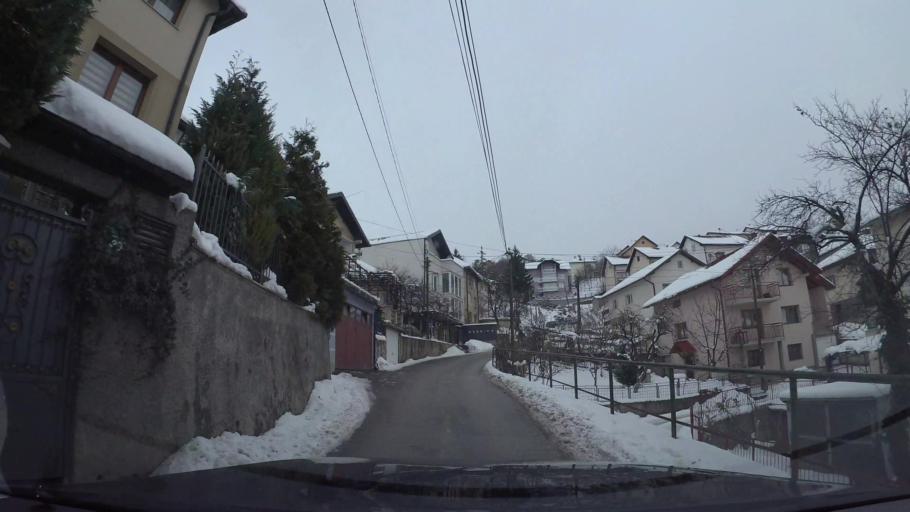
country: BA
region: Federation of Bosnia and Herzegovina
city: Kobilja Glava
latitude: 43.8637
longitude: 18.3866
